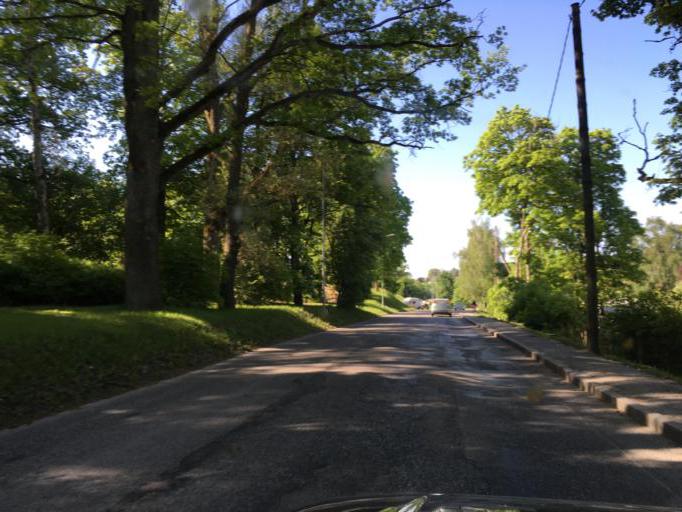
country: LV
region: Talsu Rajons
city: Talsi
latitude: 57.2426
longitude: 22.6014
